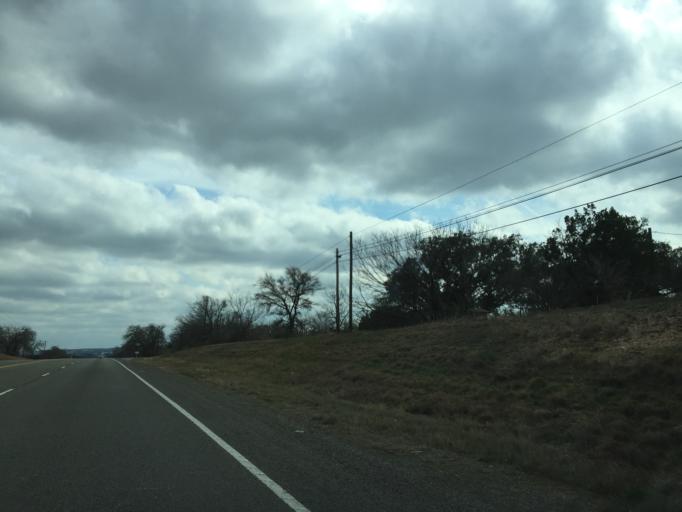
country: US
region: Texas
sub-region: Burnet County
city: Marble Falls
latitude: 30.4796
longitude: -98.1944
